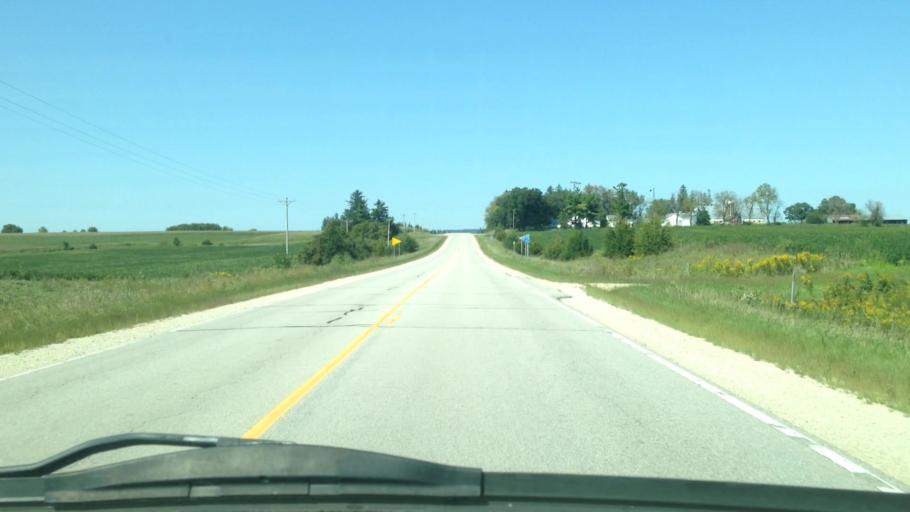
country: US
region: Minnesota
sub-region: Houston County
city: Spring Grove
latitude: 43.6234
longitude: -91.7903
